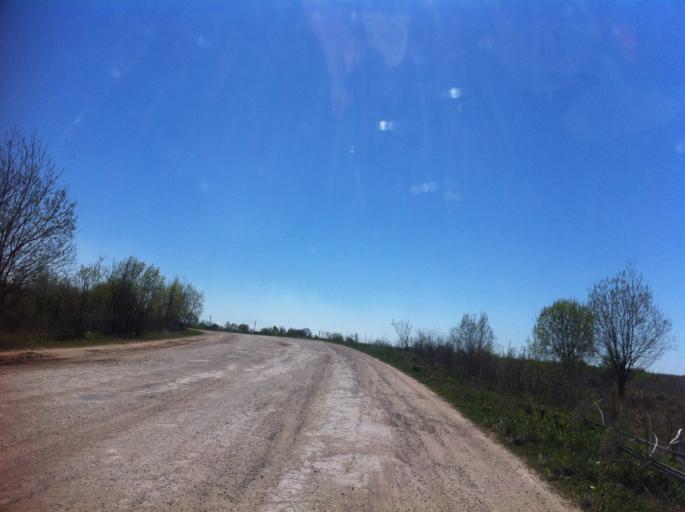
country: RU
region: Pskov
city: Izborsk
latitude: 57.7693
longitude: 27.9418
